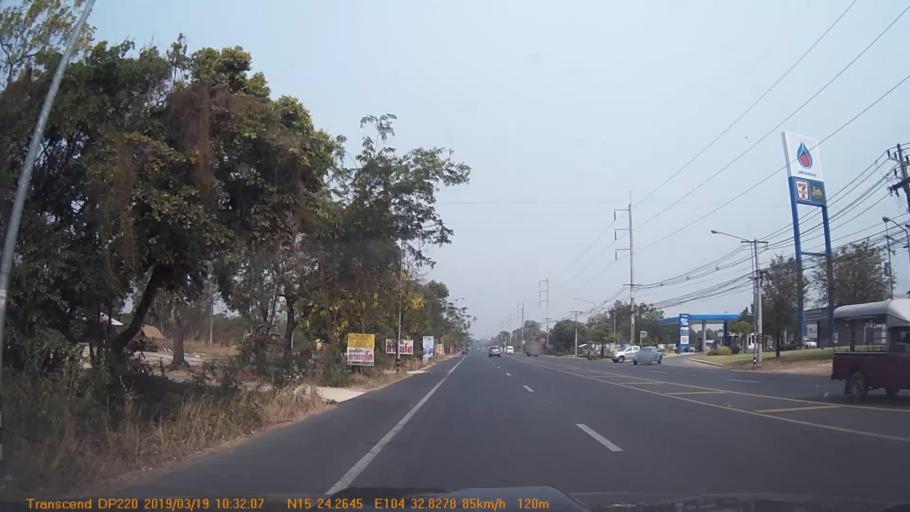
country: TH
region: Changwat Ubon Ratchathani
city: Khueang Nai
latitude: 15.4048
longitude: 104.5470
